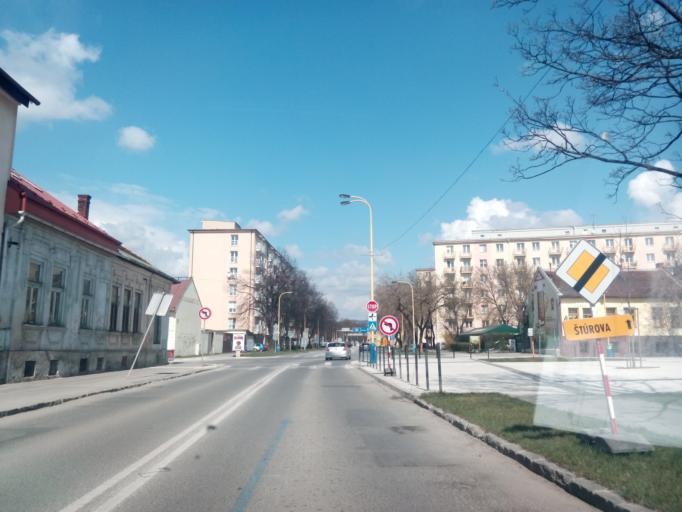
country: SK
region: Kosicky
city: Kosice
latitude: 48.7139
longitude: 21.2547
